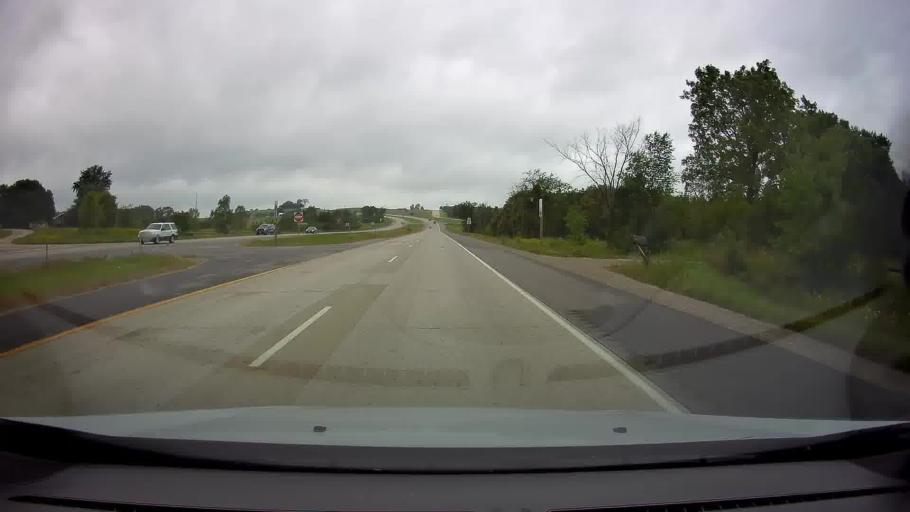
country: US
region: Wisconsin
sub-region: Shawano County
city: Bonduel
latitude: 44.7155
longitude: -88.3918
